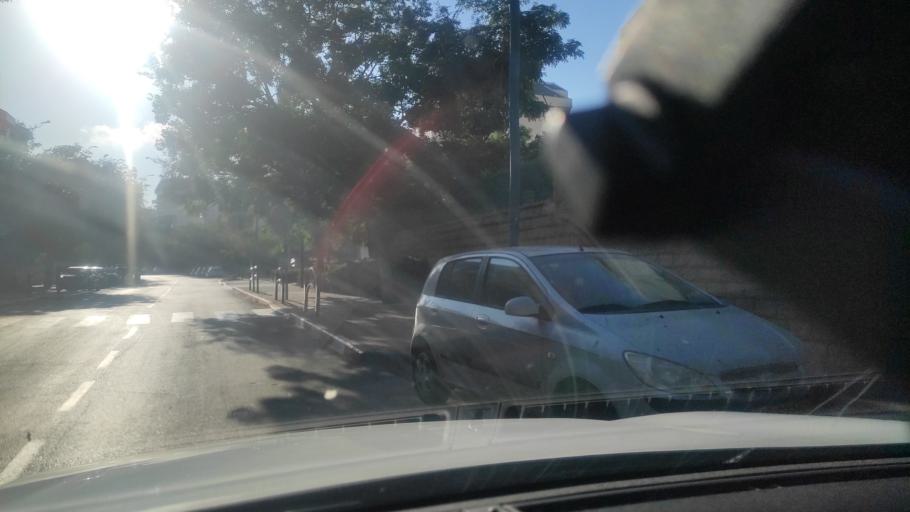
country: IL
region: Central District
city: Kfar Saba
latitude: 32.1790
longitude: 34.9343
